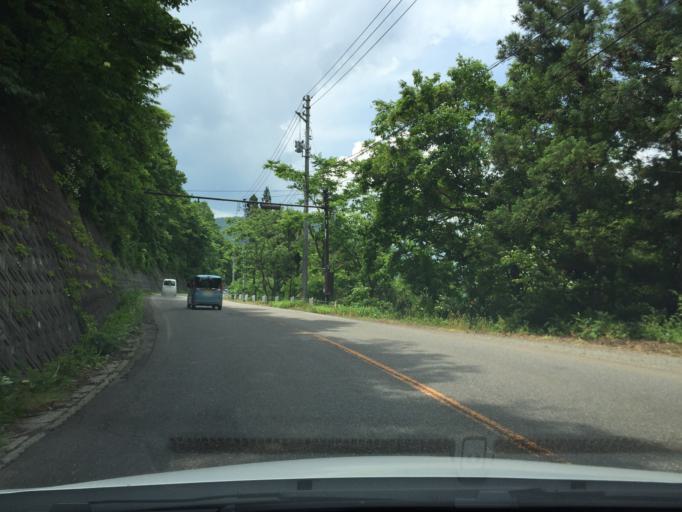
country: JP
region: Fukushima
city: Inawashiro
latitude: 37.6224
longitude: 140.1132
